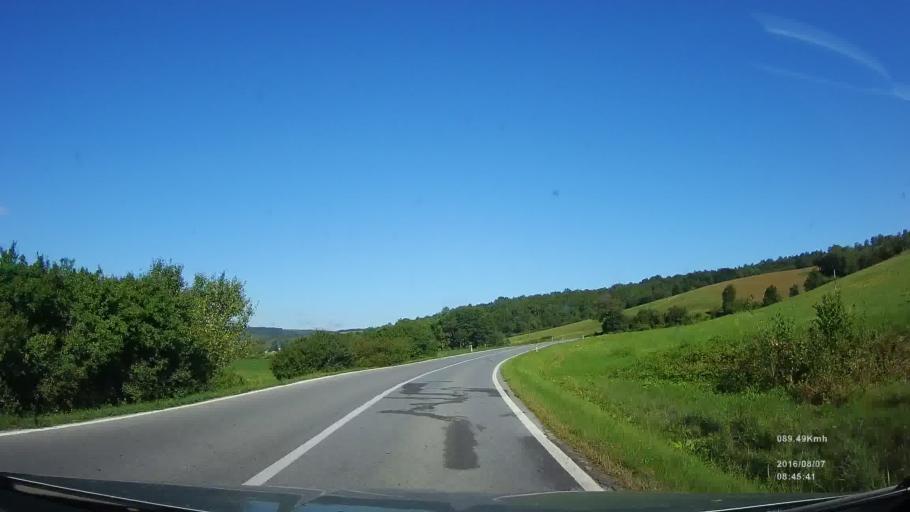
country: SK
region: Presovsky
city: Stropkov
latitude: 49.2630
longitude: 21.7364
